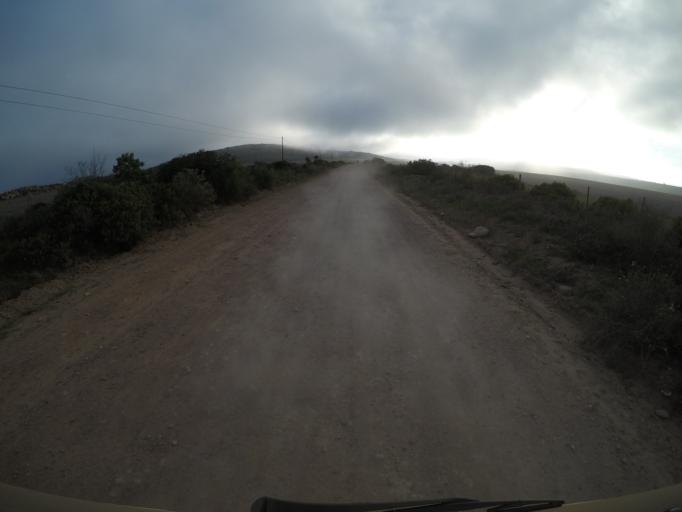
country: ZA
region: Western Cape
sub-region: Eden District Municipality
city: Mossel Bay
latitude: -34.1402
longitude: 22.0395
